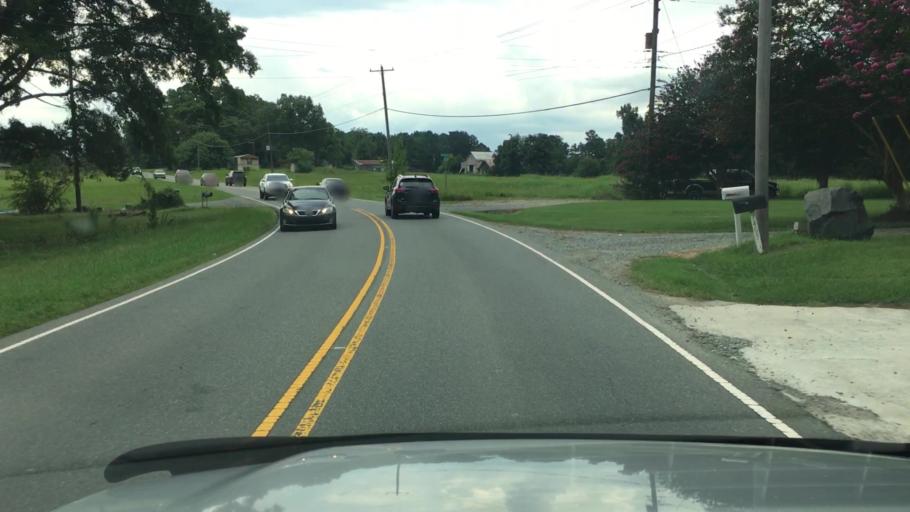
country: US
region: North Carolina
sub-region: Mecklenburg County
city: Huntersville
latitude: 35.3315
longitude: -80.8735
